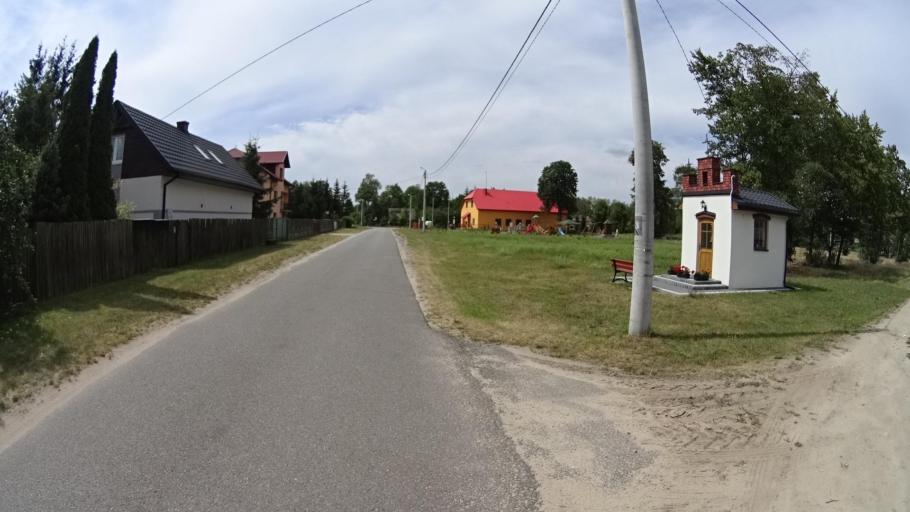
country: PL
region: Masovian Voivodeship
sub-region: Powiat bialobrzeski
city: Wysmierzyce
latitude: 51.6409
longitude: 20.8804
